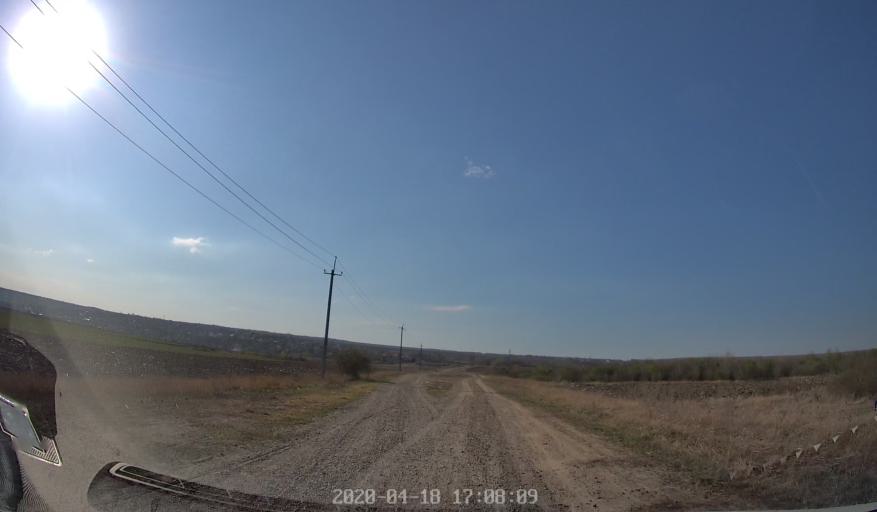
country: MD
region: Chisinau
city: Vadul lui Voda
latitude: 47.1446
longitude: 29.0919
